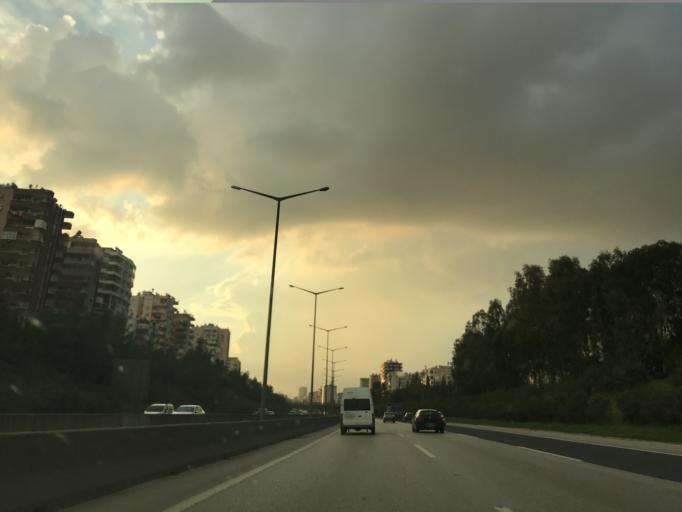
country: TR
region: Adana
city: Adana
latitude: 37.0323
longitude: 35.3052
